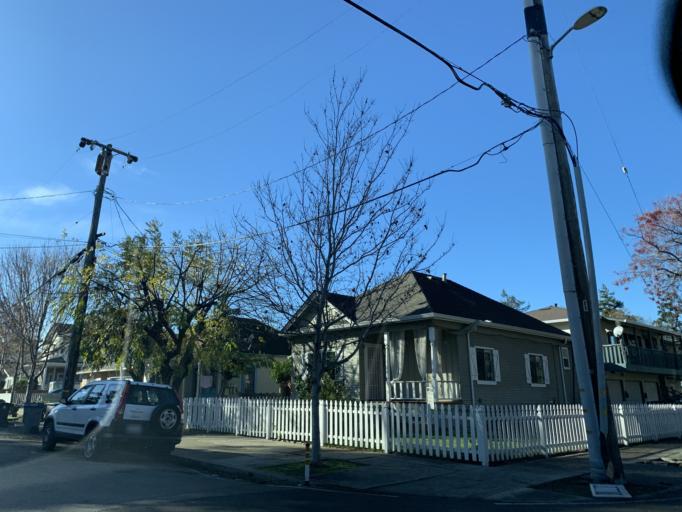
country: US
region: California
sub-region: Santa Clara County
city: Mountain View
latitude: 37.3969
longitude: -122.0867
